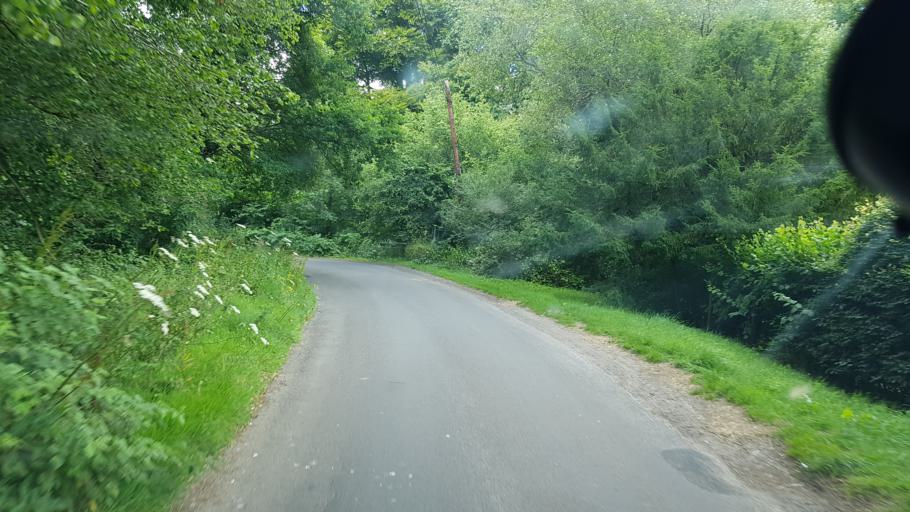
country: GB
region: England
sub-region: West Sussex
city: South Nutfield
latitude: 51.0595
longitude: -0.1211
